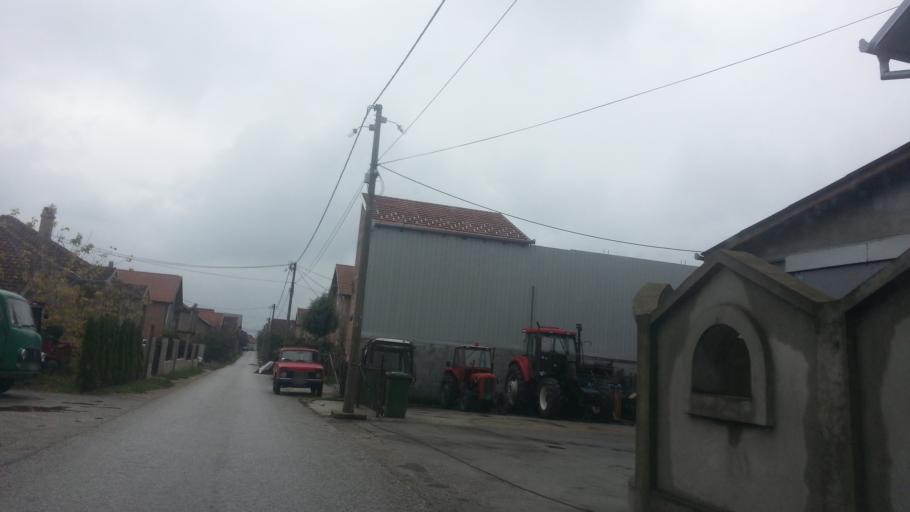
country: RS
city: Novi Banovci
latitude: 44.9106
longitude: 20.2916
